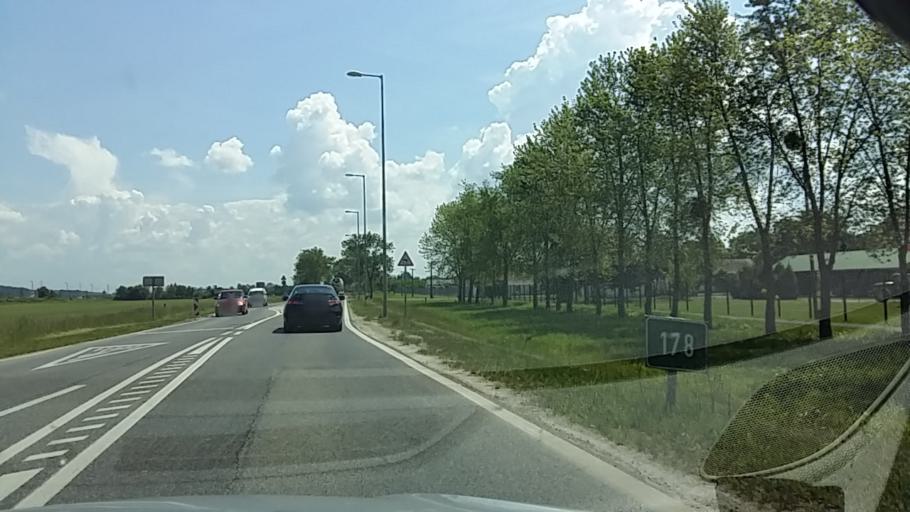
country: AT
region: Burgenland
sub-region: Politischer Bezirk Gussing
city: Heiligenbrunn
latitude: 46.9668
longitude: 16.4335
